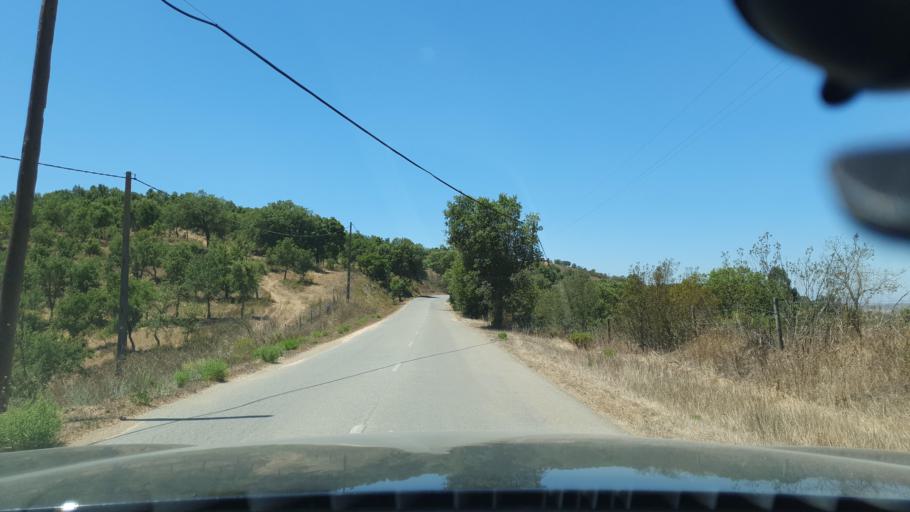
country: PT
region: Beja
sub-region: Odemira
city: Odemira
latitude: 37.5507
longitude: -8.4236
